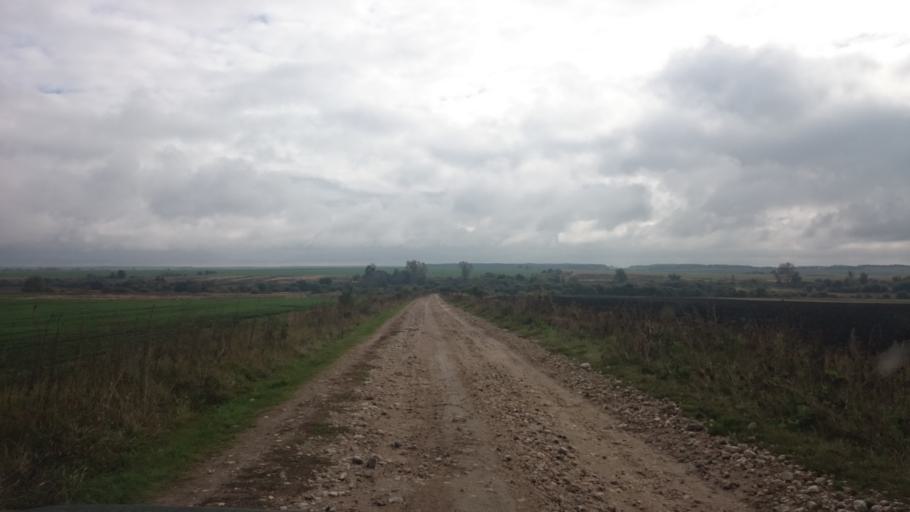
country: RU
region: Mordoviya
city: Kadoshkino
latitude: 54.0200
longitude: 44.4473
